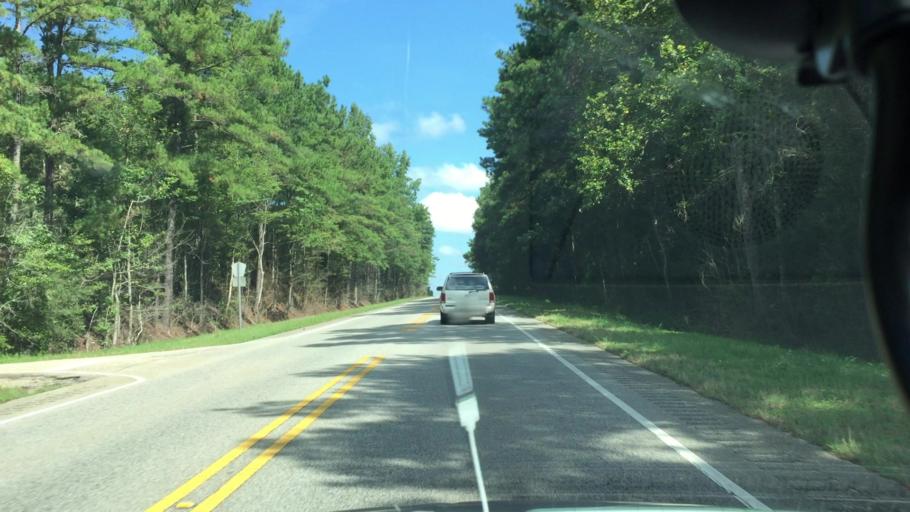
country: US
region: Alabama
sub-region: Coffee County
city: New Brockton
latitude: 31.4074
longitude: -85.8825
